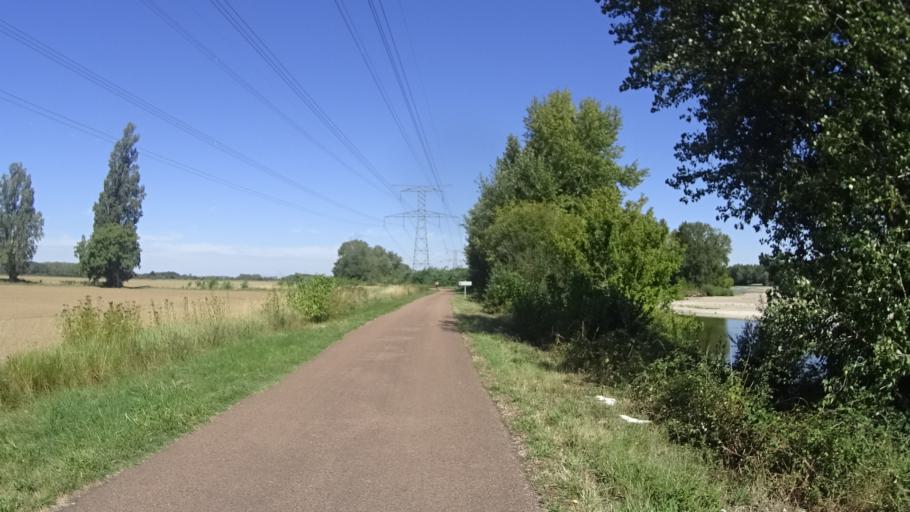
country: FR
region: Centre
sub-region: Departement du Cher
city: Lere
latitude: 47.4851
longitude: 2.8957
